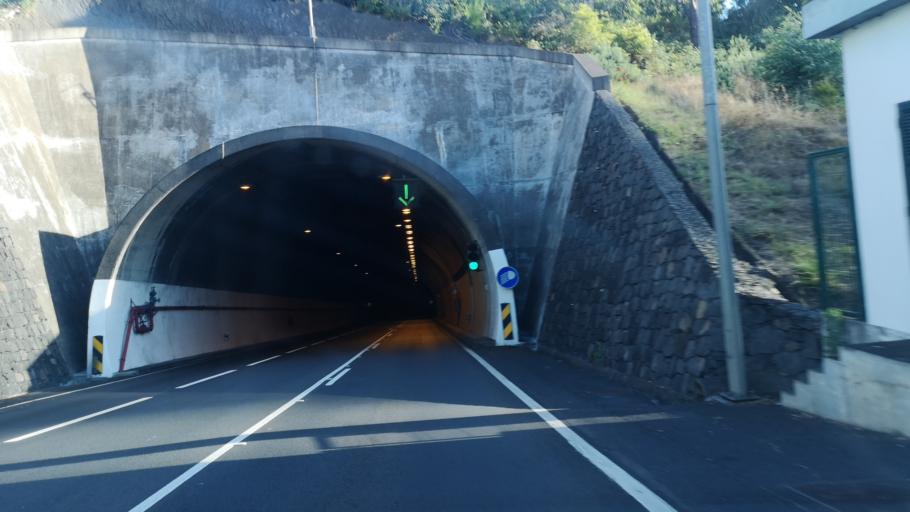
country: PT
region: Madeira
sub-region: Santa Cruz
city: Camacha
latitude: 32.6736
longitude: -16.8480
